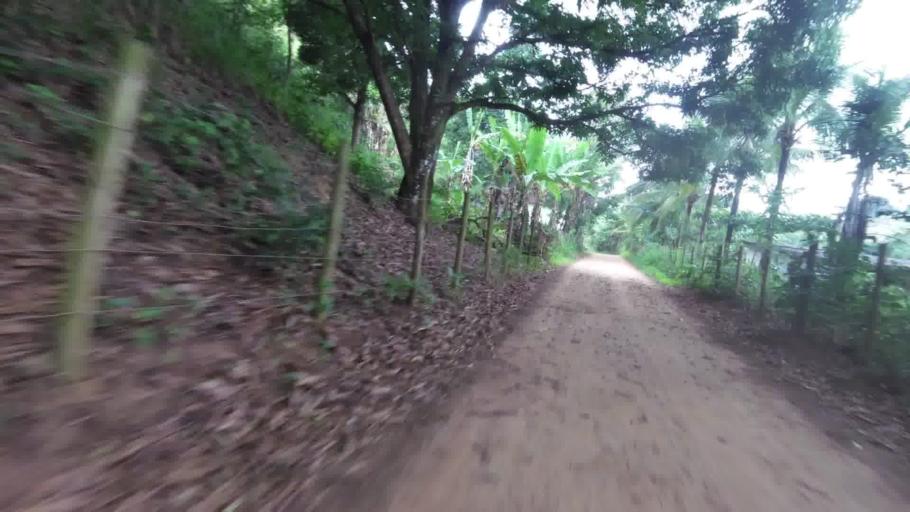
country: BR
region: Espirito Santo
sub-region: Alfredo Chaves
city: Alfredo Chaves
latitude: -20.6304
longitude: -40.7540
